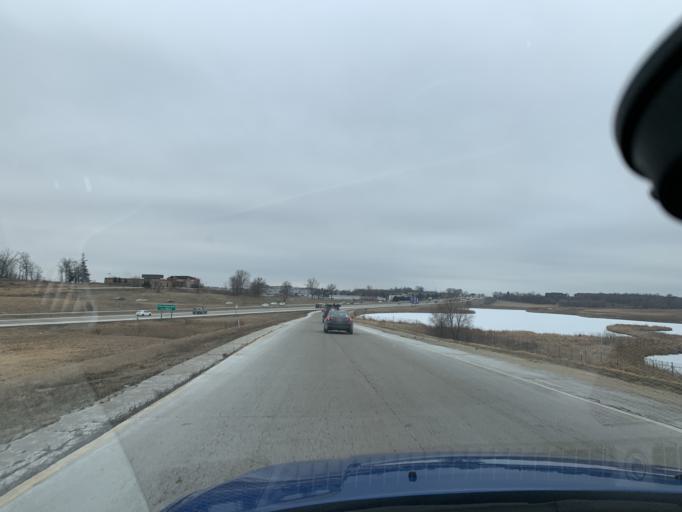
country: US
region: Wisconsin
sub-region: Dane County
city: Sun Prairie
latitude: 43.1621
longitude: -89.2686
